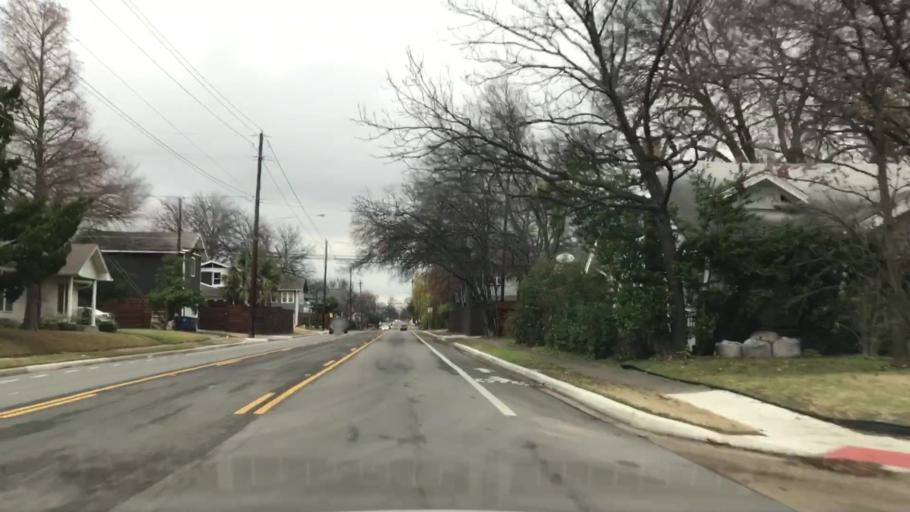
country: US
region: Texas
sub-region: Dallas County
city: Highland Park
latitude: 32.8198
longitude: -96.7680
